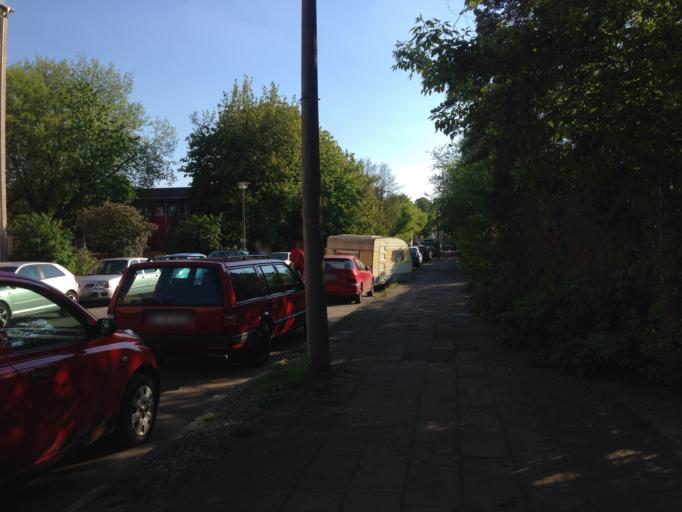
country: DE
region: Berlin
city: Pankow
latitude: 52.5753
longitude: 13.4162
